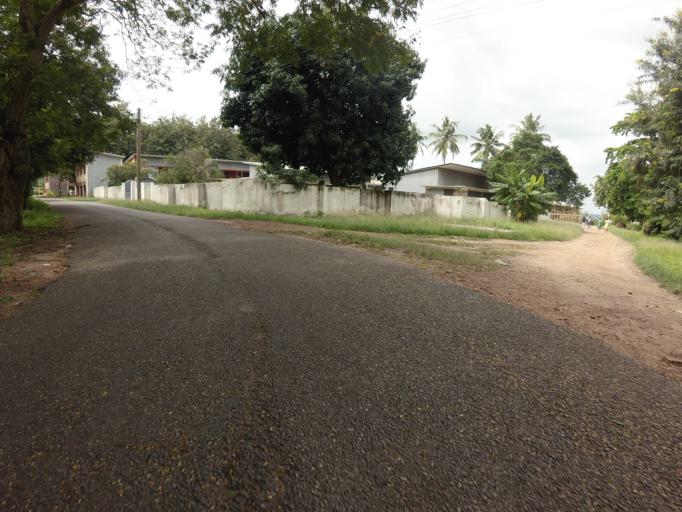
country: GH
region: Volta
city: Ho
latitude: 6.5959
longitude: 0.4751
